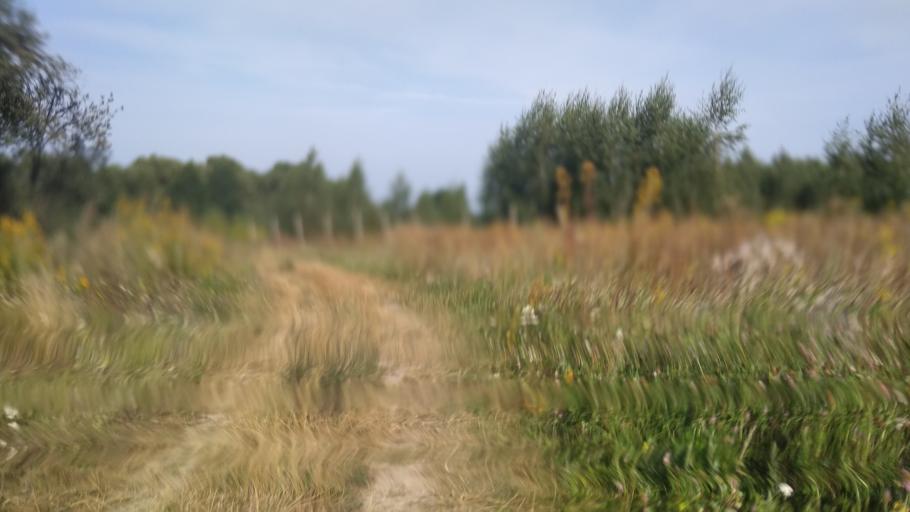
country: PL
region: Kujawsko-Pomorskie
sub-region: Powiat bydgoski
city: Osielsko
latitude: 53.2254
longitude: 18.1506
